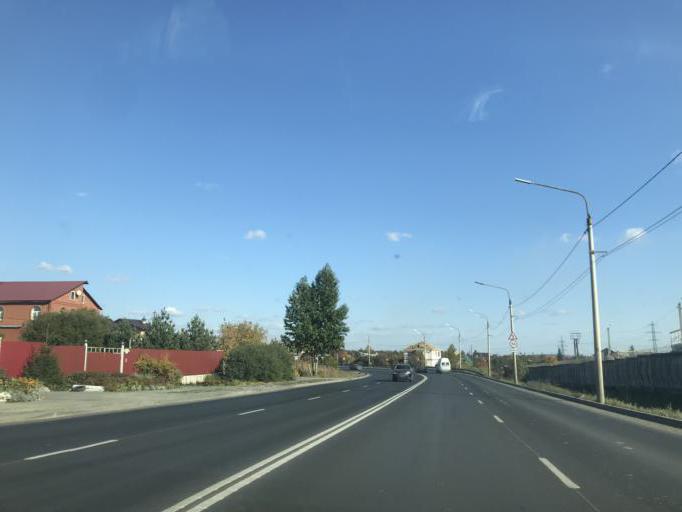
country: RU
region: Chelyabinsk
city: Roshchino
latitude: 55.2351
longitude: 61.3144
